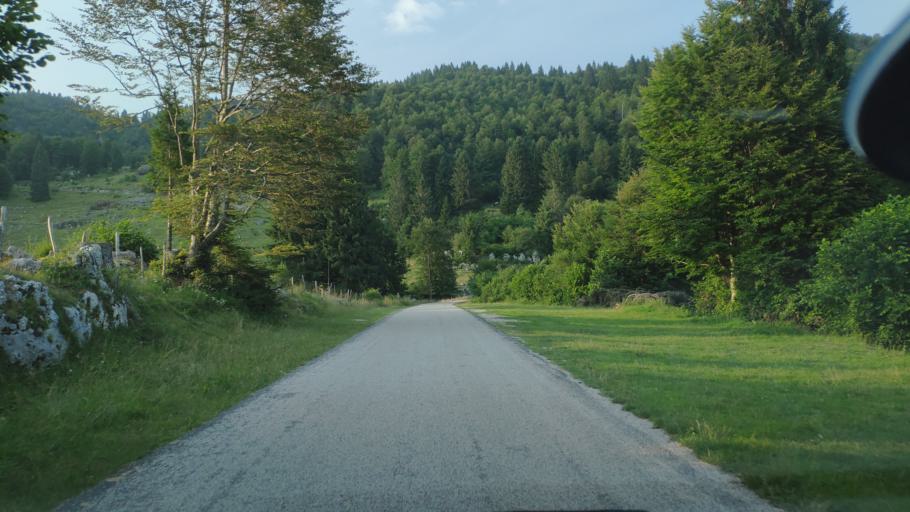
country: IT
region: Veneto
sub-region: Provincia di Vicenza
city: Calvene
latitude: 45.7979
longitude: 11.4929
